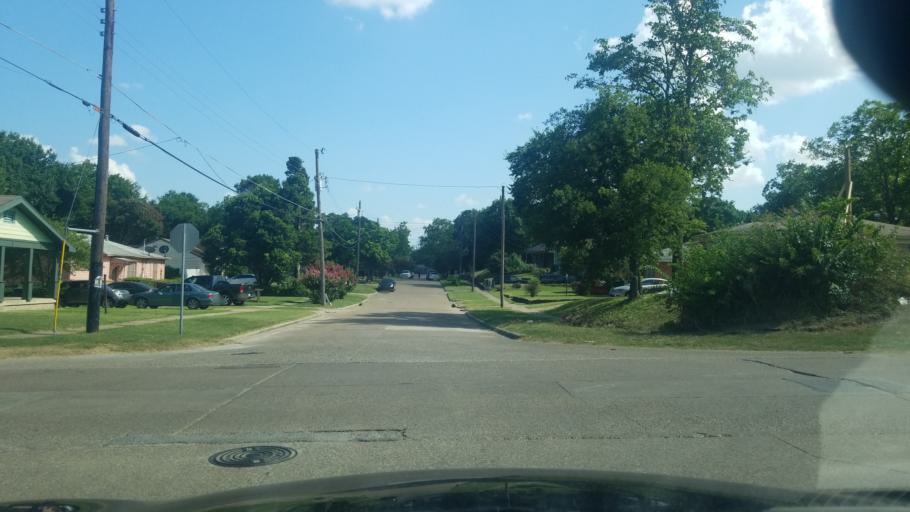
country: US
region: Texas
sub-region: Dallas County
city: Dallas
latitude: 32.7296
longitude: -96.8103
